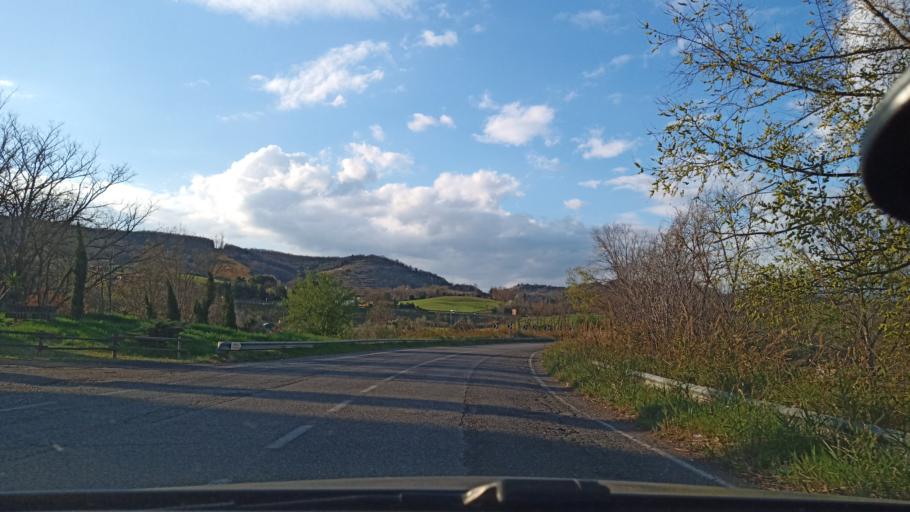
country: IT
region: Latium
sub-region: Citta metropolitana di Roma Capitale
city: Fiano Romano
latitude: 42.1804
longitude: 12.6054
